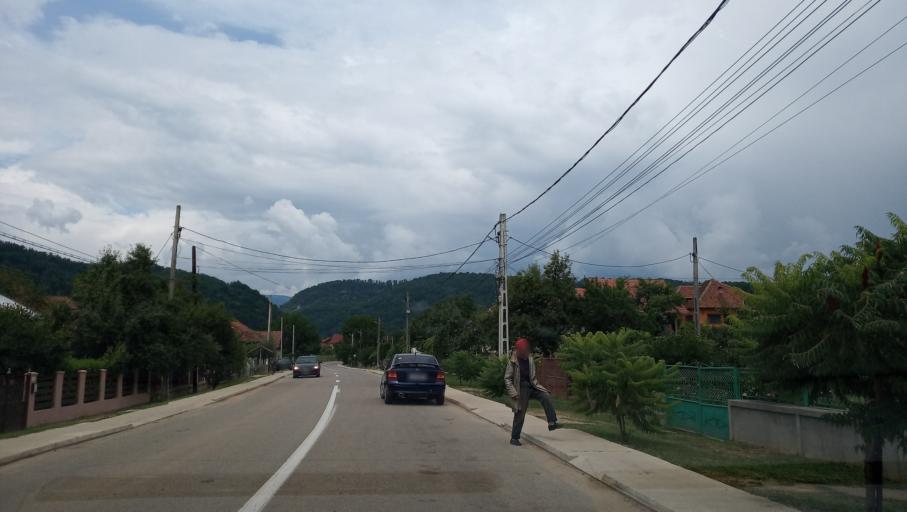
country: RO
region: Gorj
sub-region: Comuna Tismana
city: Tismana
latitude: 45.0582
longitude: 22.9455
